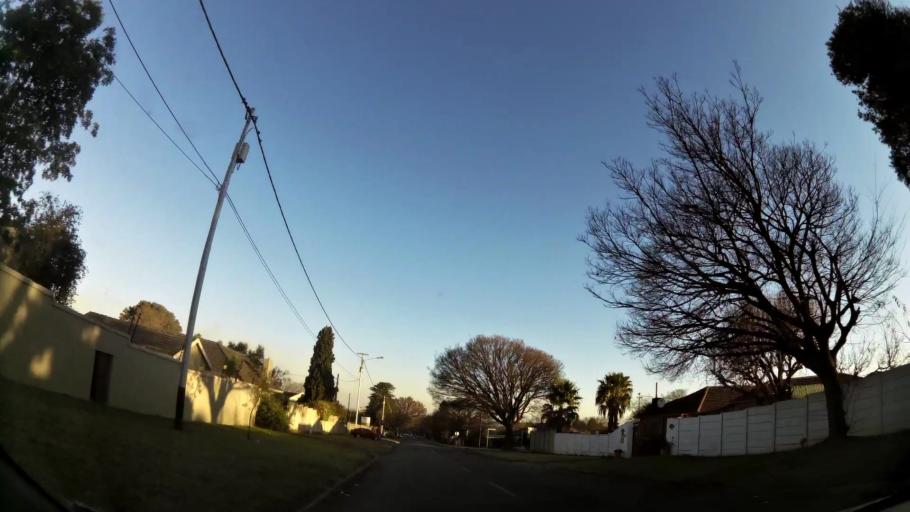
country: ZA
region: Gauteng
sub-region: City of Johannesburg Metropolitan Municipality
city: Roodepoort
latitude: -26.1518
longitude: 27.8846
